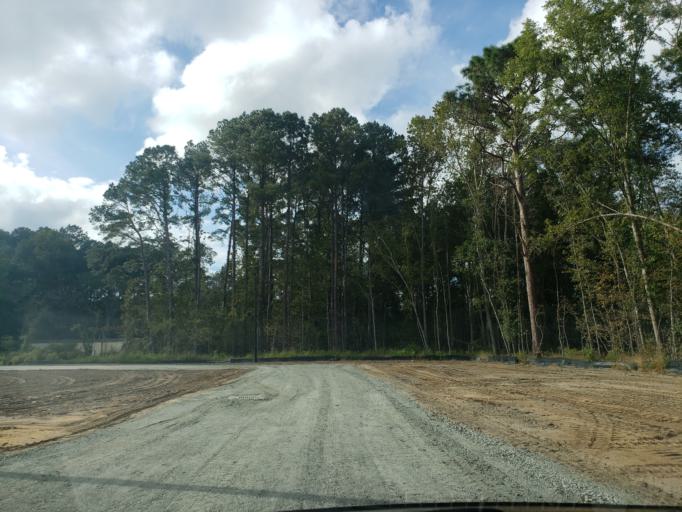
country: US
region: Georgia
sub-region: Bryan County
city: Richmond Hill
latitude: 32.0078
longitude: -81.2950
